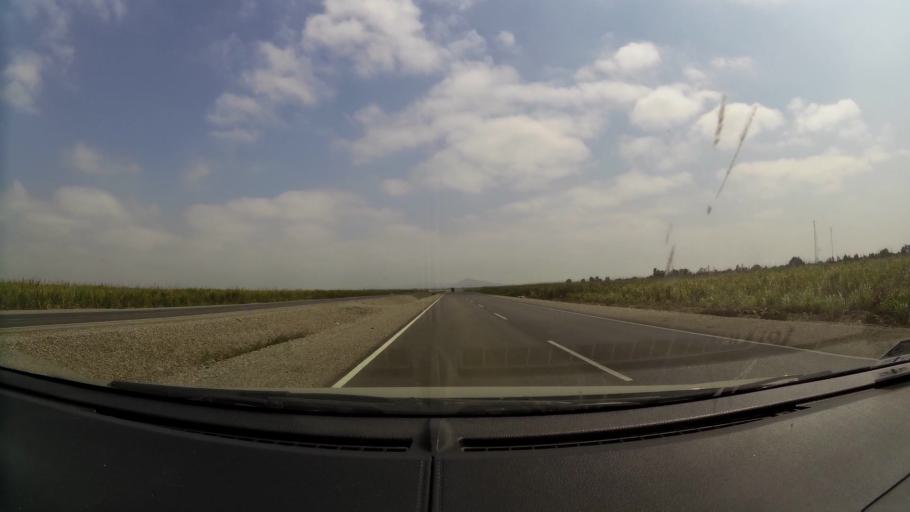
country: PE
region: La Libertad
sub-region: Ascope
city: Chicama
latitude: -7.8555
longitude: -79.1463
